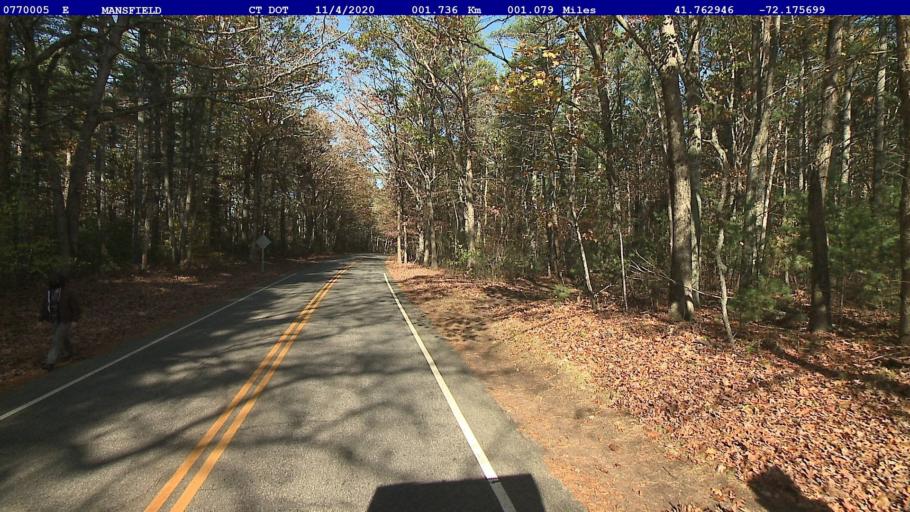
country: US
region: Connecticut
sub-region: Tolland County
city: Mansfield City
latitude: 41.7630
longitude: -72.1757
